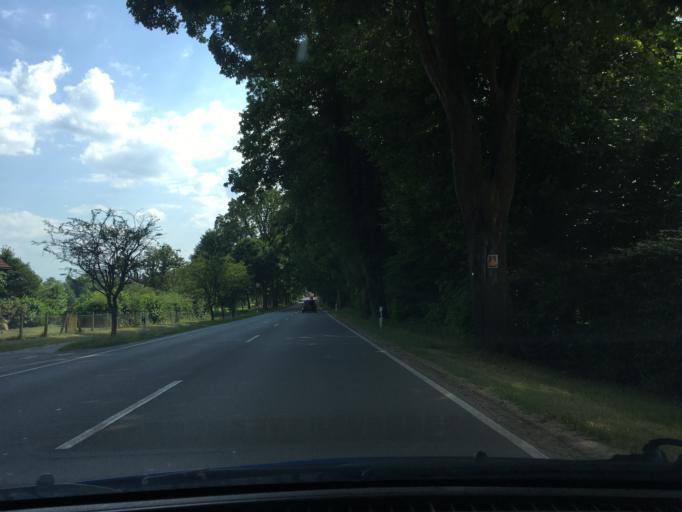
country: DE
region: Lower Saxony
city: Welle
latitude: 53.2452
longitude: 9.8055
